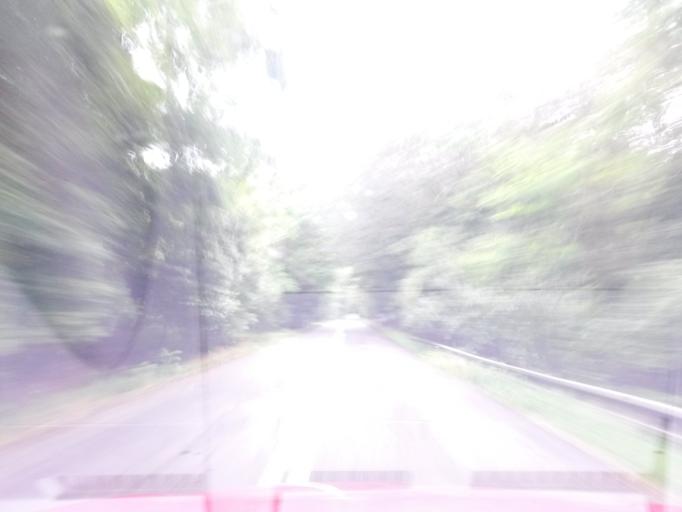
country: SK
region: Nitriansky
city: Sahy
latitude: 48.1686
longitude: 19.0285
